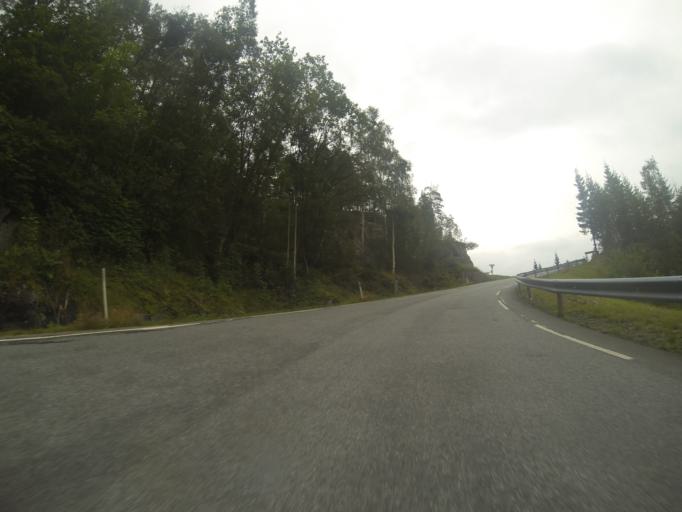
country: NO
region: Rogaland
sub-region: Suldal
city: Sand
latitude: 59.5098
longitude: 6.2092
